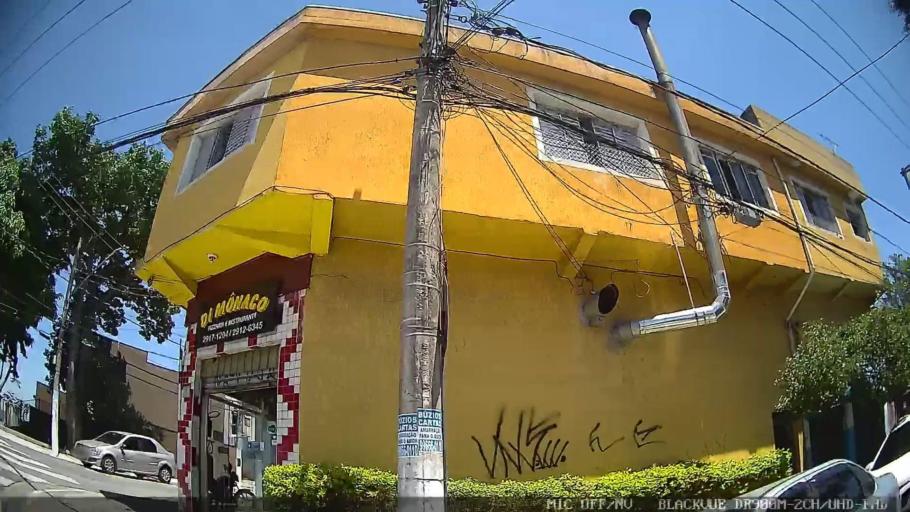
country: BR
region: Sao Paulo
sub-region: Sao Caetano Do Sul
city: Sao Caetano do Sul
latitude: -23.6009
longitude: -46.5573
